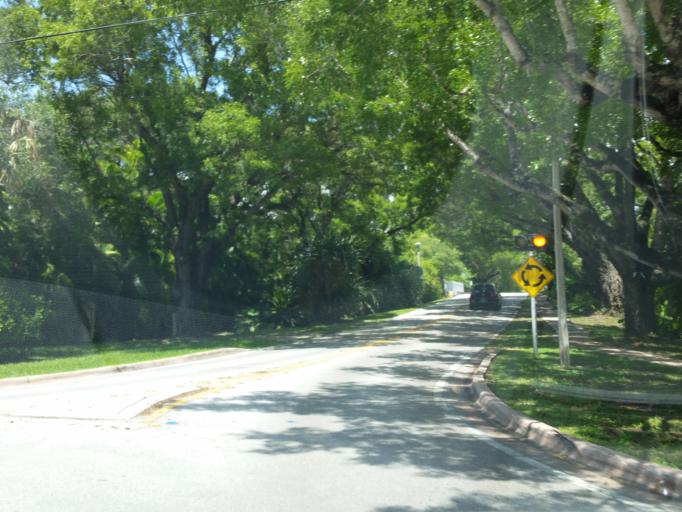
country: US
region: Florida
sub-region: Miami-Dade County
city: Coral Gables
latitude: 25.7125
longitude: -80.2664
